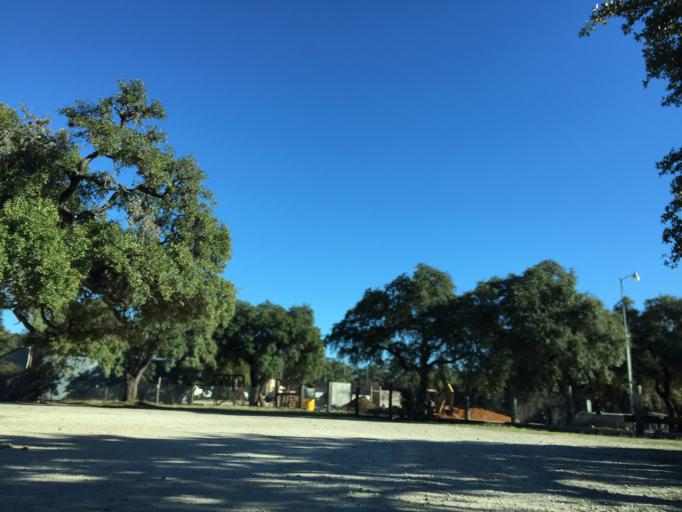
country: US
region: Texas
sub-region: Bexar County
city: Castle Hills
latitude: 29.5551
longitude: -98.4981
